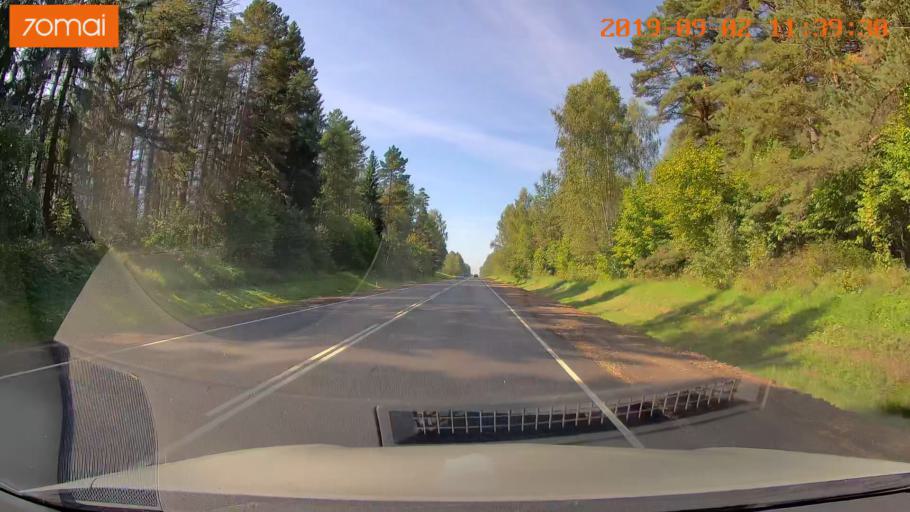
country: RU
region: Smolensk
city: Oster
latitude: 53.9076
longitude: 32.7218
